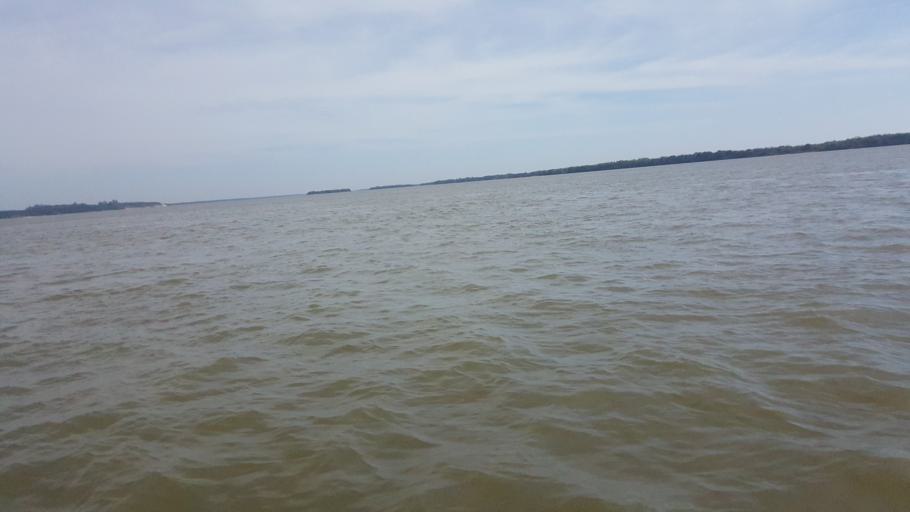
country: AR
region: Corrientes
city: Ituzaingo
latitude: -27.6061
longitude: -56.8275
